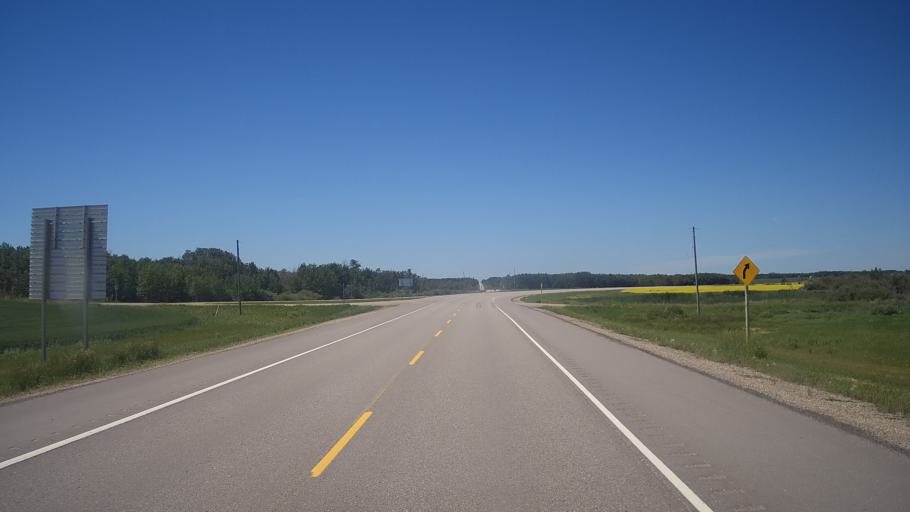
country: CA
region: Manitoba
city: Minnedosa
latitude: 50.2702
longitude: -99.9290
